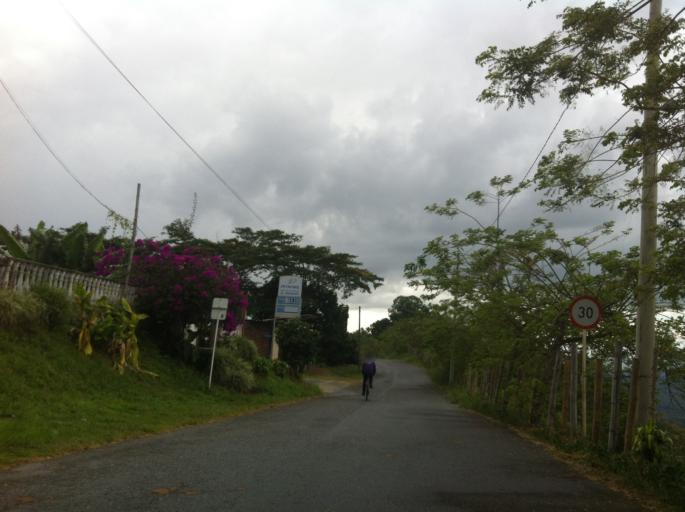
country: CO
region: Quindio
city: Buenavista
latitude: 4.3636
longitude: -75.7444
